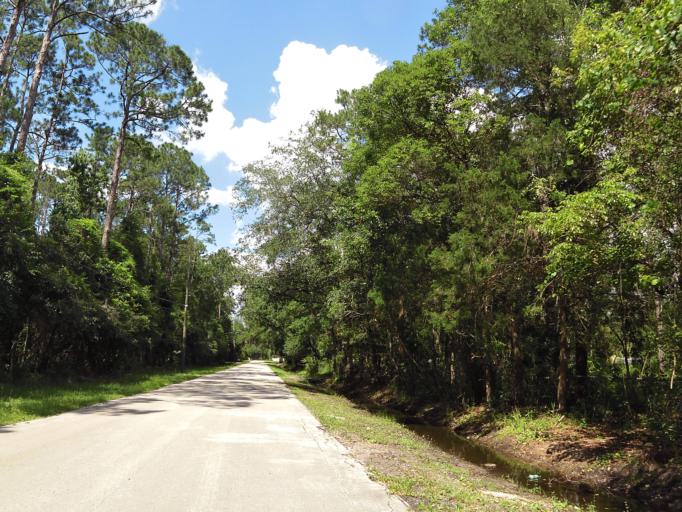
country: US
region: Florida
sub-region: Saint Johns County
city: Fruit Cove
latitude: 30.1446
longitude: -81.5166
